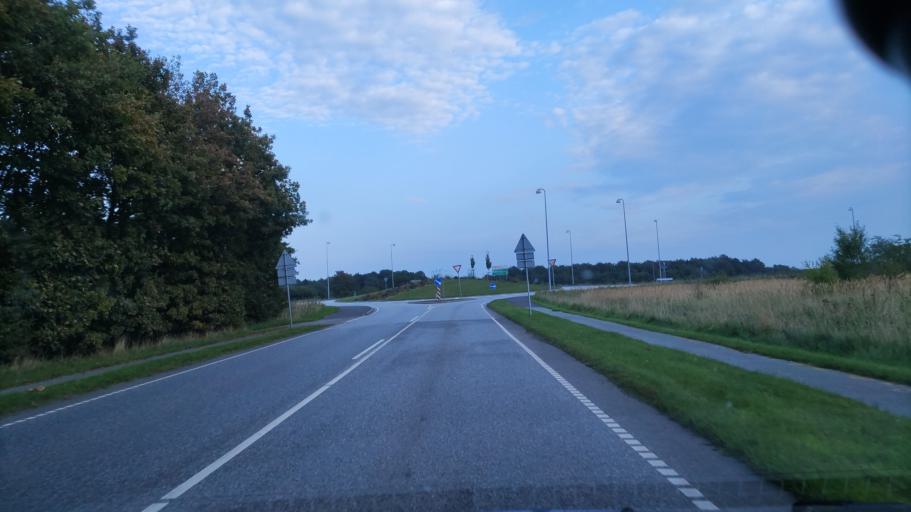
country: DK
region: South Denmark
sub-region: Aabenraa Kommune
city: Padborg
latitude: 54.8597
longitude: 9.3571
